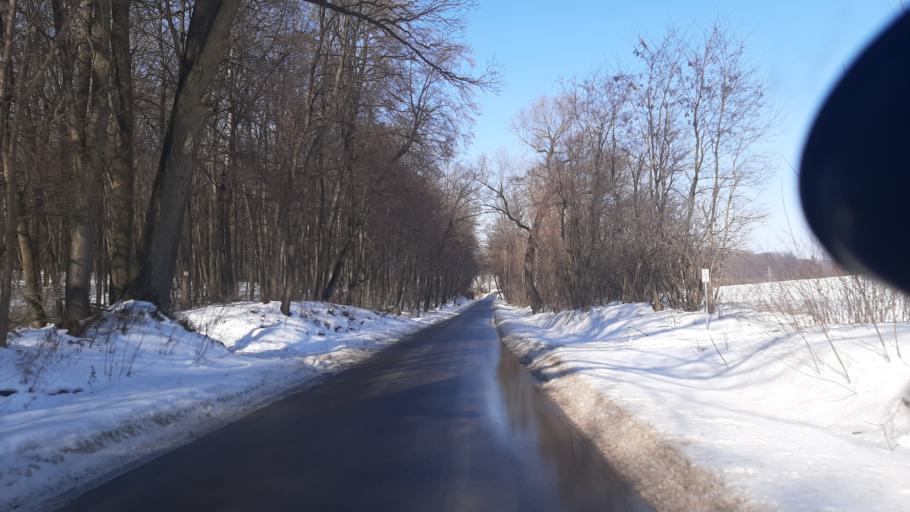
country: PL
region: Lublin Voivodeship
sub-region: Powiat pulawski
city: Naleczow
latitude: 51.2942
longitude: 22.2670
